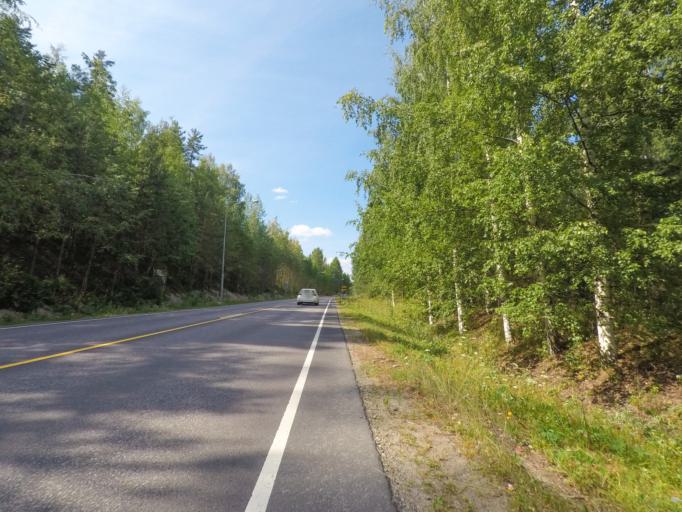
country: FI
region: Southern Savonia
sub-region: Mikkeli
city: Puumala
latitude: 61.5140
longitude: 28.1756
